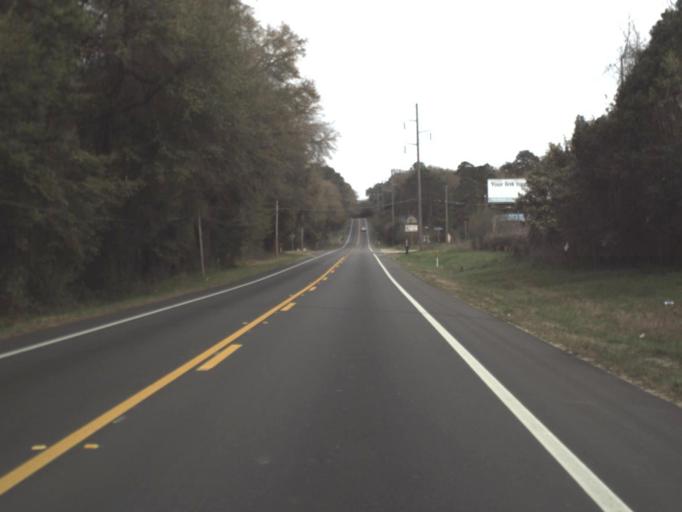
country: US
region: Florida
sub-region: Leon County
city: Tallahassee
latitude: 30.4355
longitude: -84.3713
